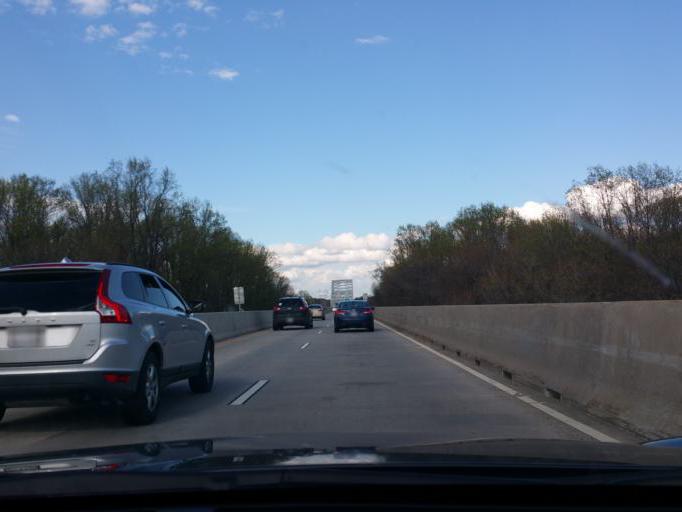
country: US
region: Maryland
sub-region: Harford County
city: Havre de Grace
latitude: 39.5612
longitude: -76.0887
